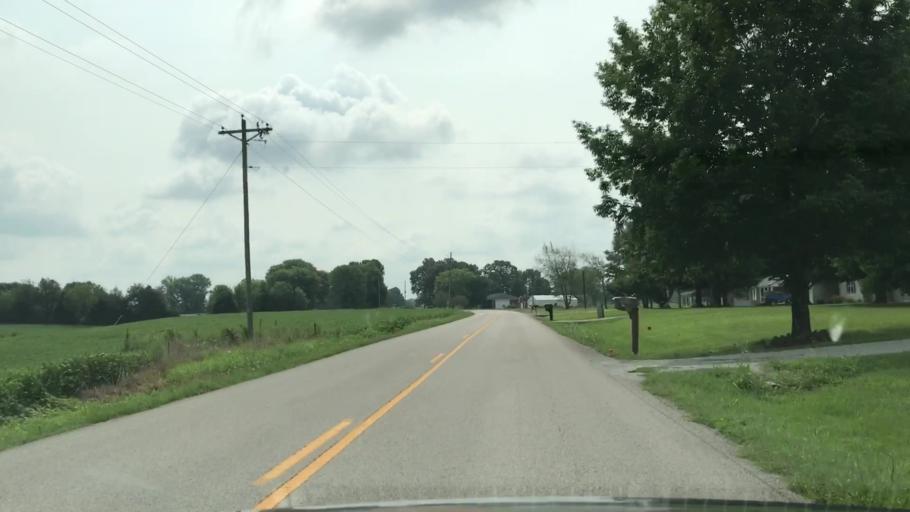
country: US
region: Kentucky
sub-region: Edmonson County
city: Brownsville
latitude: 37.1351
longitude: -86.1744
